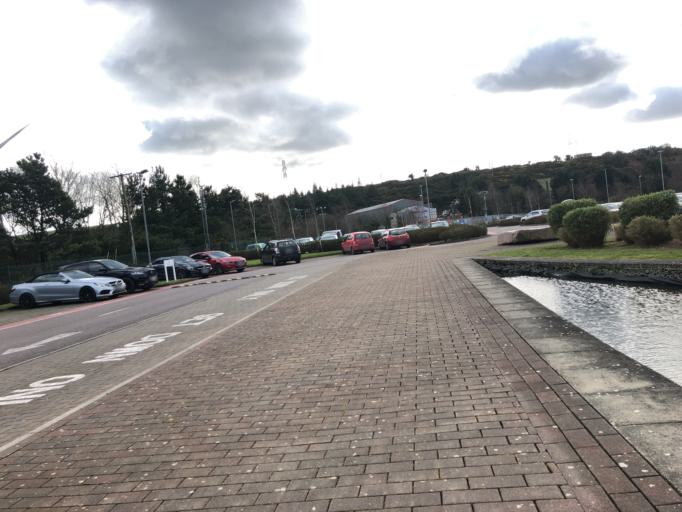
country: IE
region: Munster
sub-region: County Cork
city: Cobh
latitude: 51.8325
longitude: -8.3048
